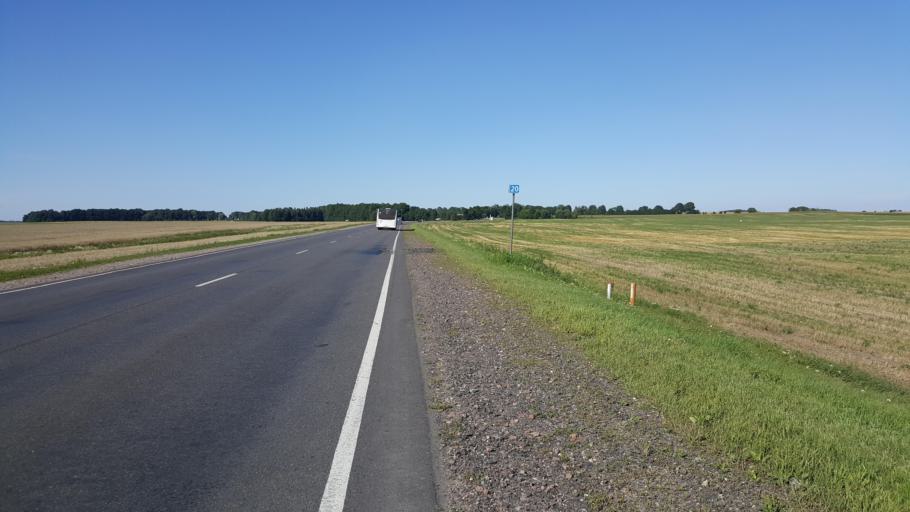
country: BY
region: Brest
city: Charnawchytsy
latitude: 52.2542
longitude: 23.7543
